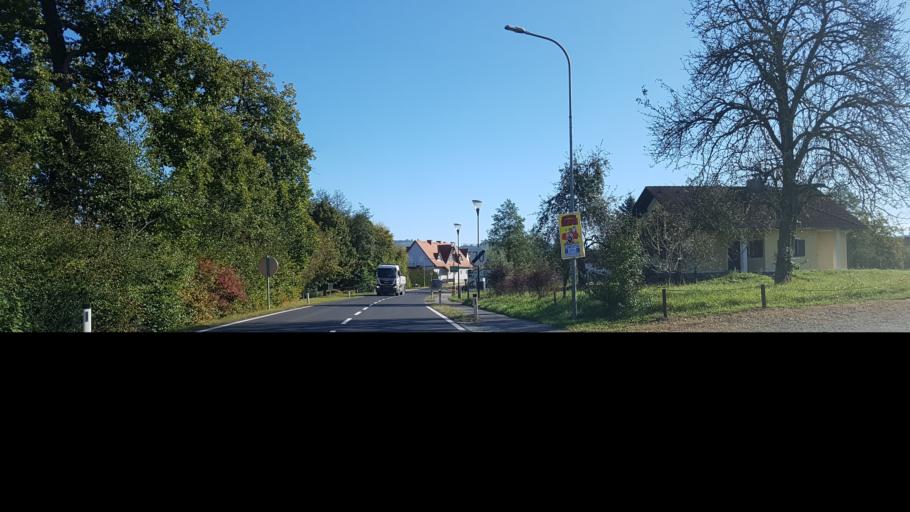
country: AT
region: Styria
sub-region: Politischer Bezirk Leibnitz
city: Gleinstatten
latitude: 46.7549
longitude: 15.3663
